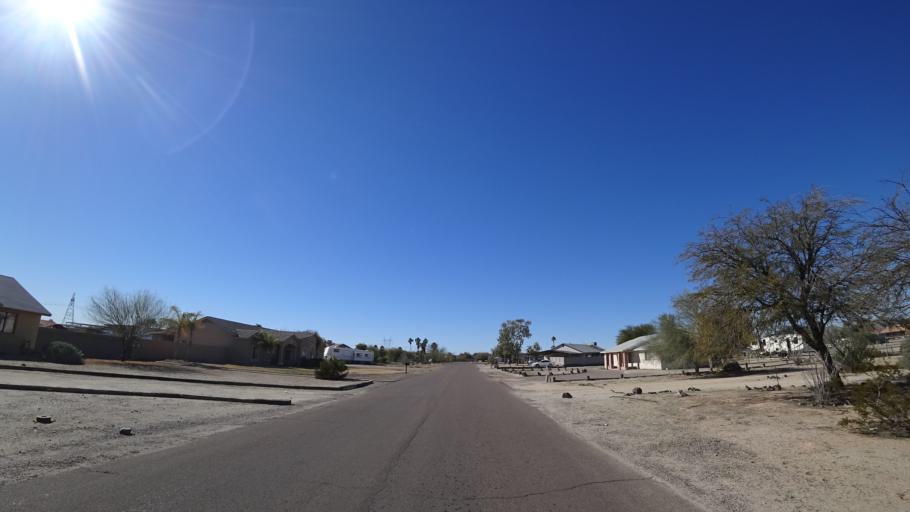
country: US
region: Arizona
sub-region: Maricopa County
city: Buckeye
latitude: 33.4259
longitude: -112.5289
